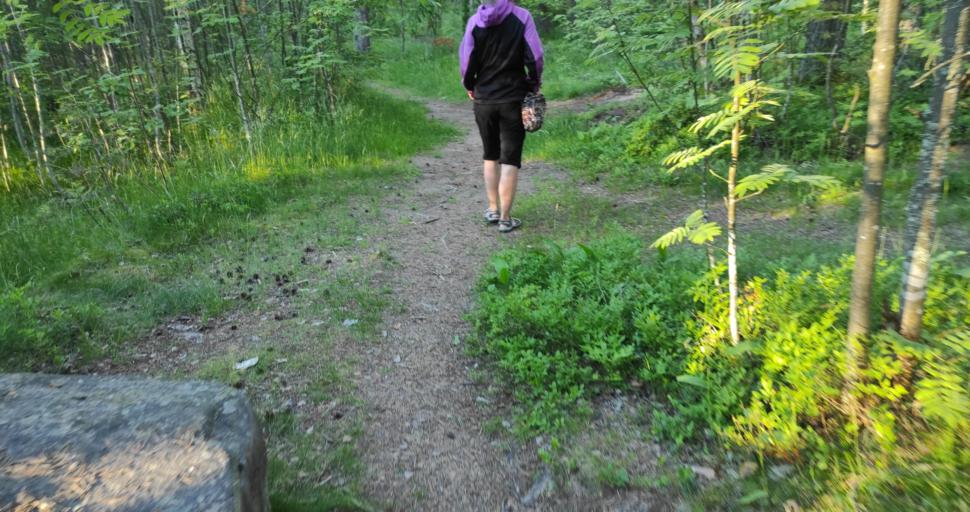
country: RU
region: Leningrad
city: Sosnovyy Bor
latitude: 60.1624
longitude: 29.1474
